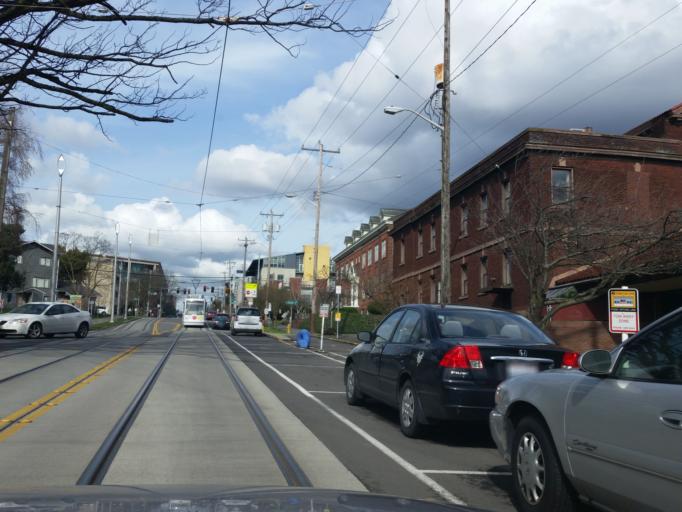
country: US
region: Washington
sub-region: King County
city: Seattle
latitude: 47.6030
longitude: -122.3208
